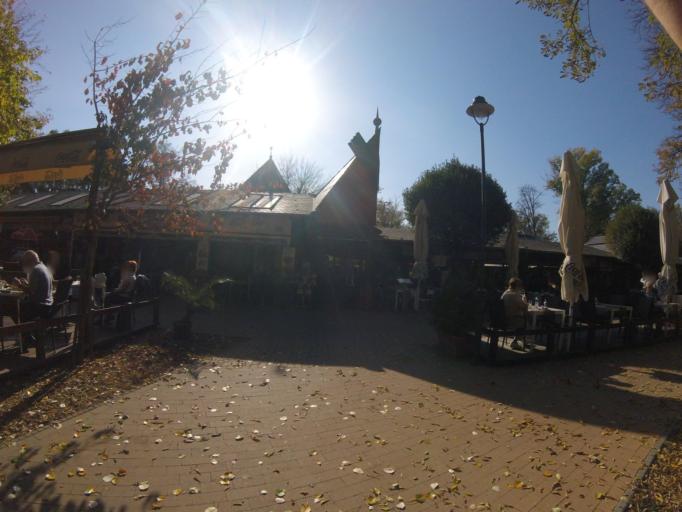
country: HU
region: Zala
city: Keszthely
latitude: 46.7591
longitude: 17.2513
